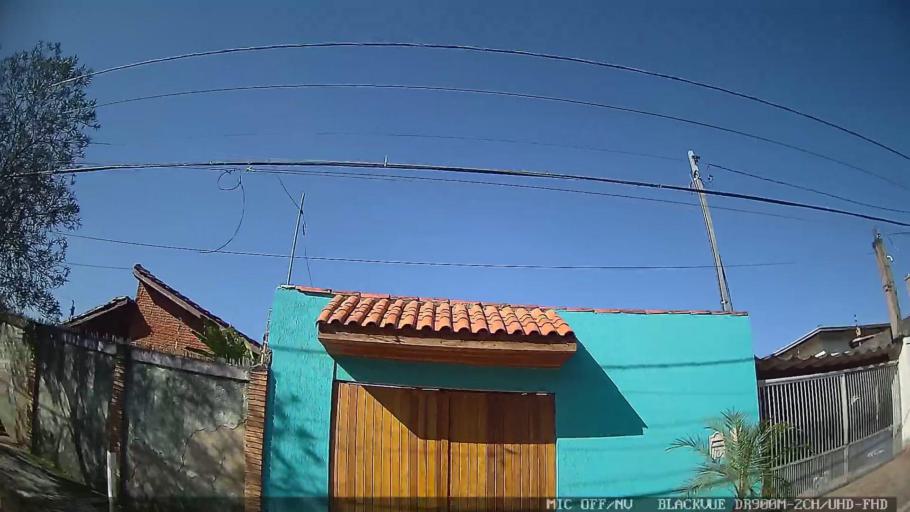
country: BR
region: Sao Paulo
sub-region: Guaruja
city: Guaruja
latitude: -23.9743
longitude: -46.2109
